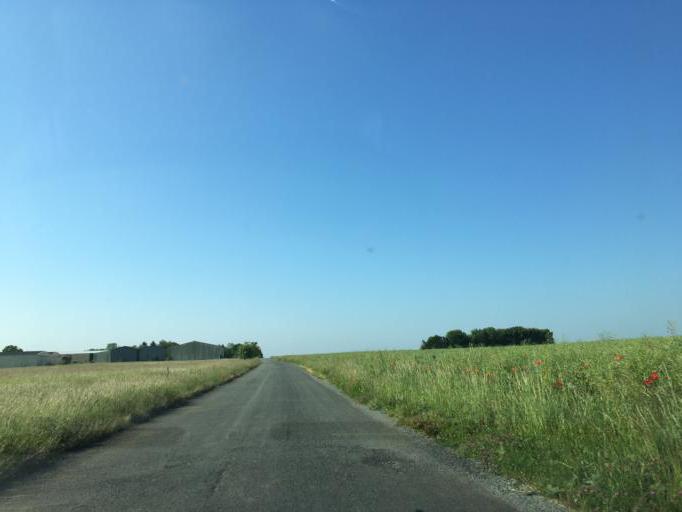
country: FR
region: Poitou-Charentes
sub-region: Departement des Deux-Sevres
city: Beauvoir-sur-Niort
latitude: 46.0871
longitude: -0.5066
